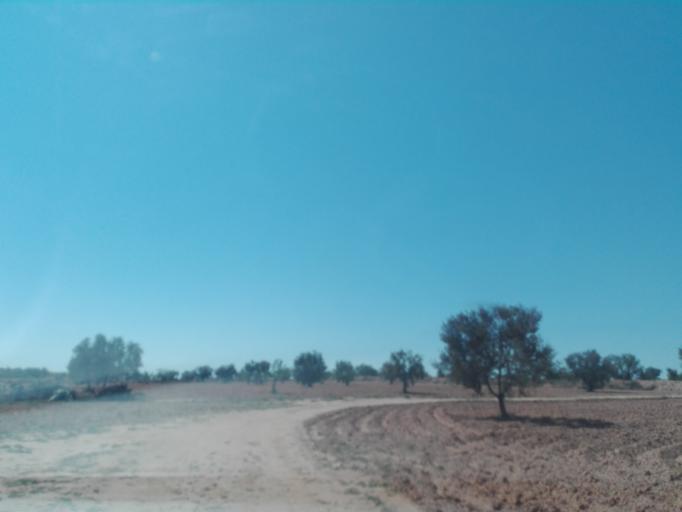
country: TN
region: Safaqis
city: Bi'r `Ali Bin Khalifah
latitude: 34.7971
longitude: 10.2843
